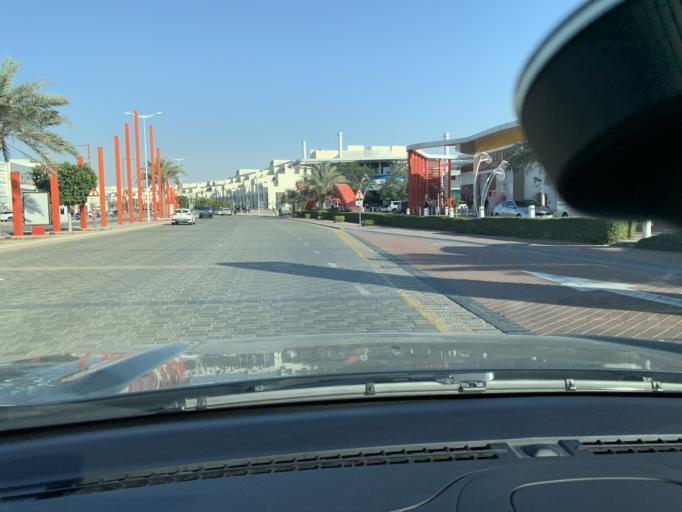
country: AE
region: Dubai
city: Dubai
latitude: 25.0462
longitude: 55.2393
